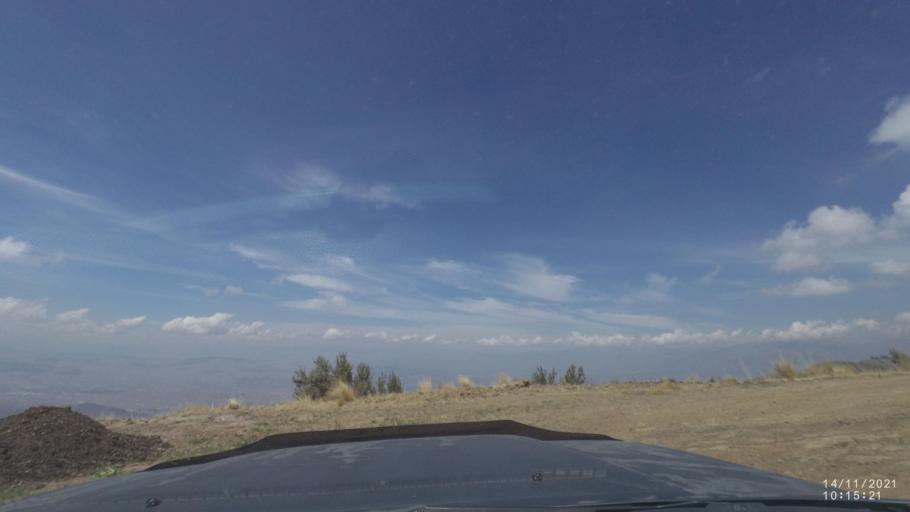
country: BO
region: Cochabamba
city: Cochabamba
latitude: -17.3435
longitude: -66.0877
